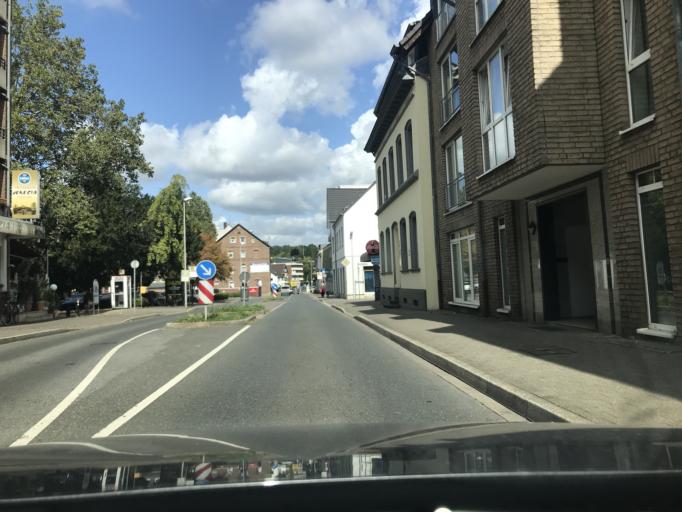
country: DE
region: North Rhine-Westphalia
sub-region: Regierungsbezirk Dusseldorf
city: Erkrath
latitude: 51.2228
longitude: 6.9127
